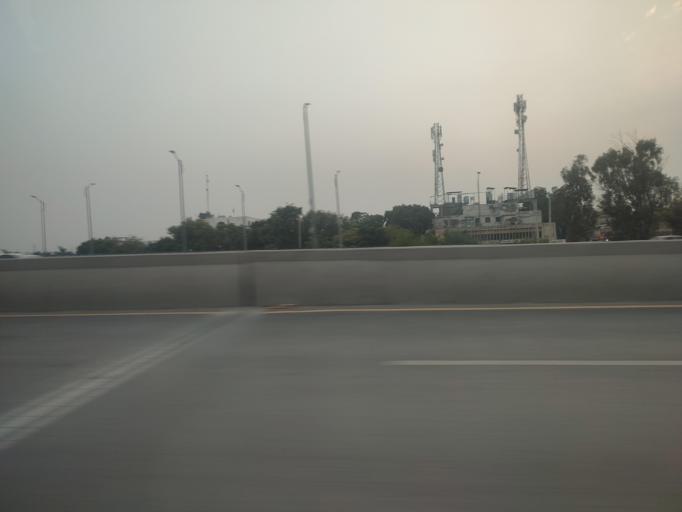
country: PK
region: Islamabad
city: Islamabad
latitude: 33.6864
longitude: 73.0464
